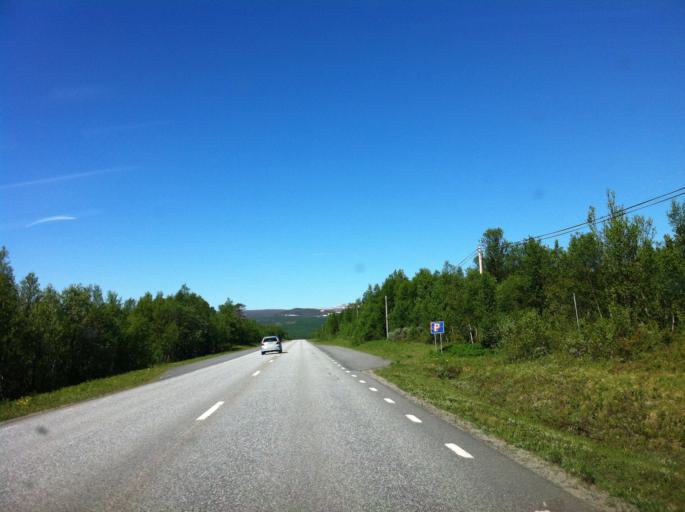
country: NO
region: Hedmark
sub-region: Engerdal
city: Engerdal
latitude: 62.5353
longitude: 12.3955
